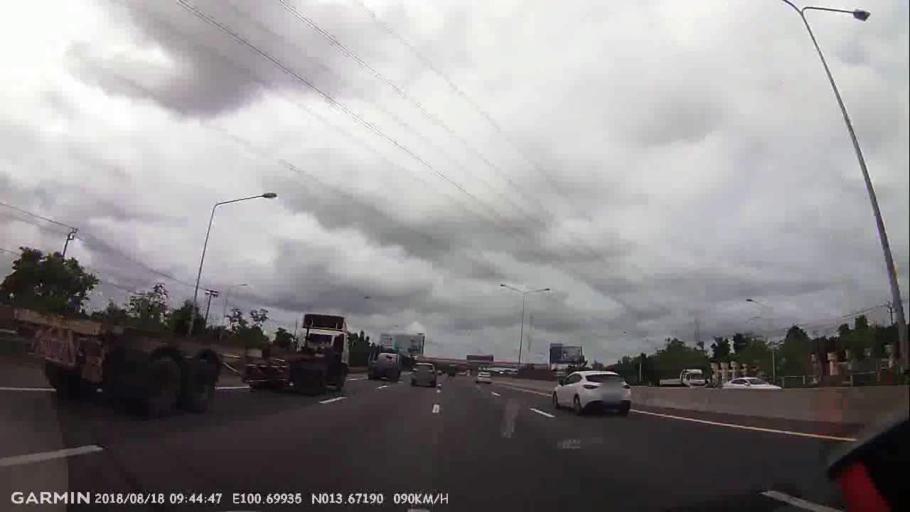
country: TH
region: Bangkok
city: Bang Na
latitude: 13.6720
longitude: 100.6996
